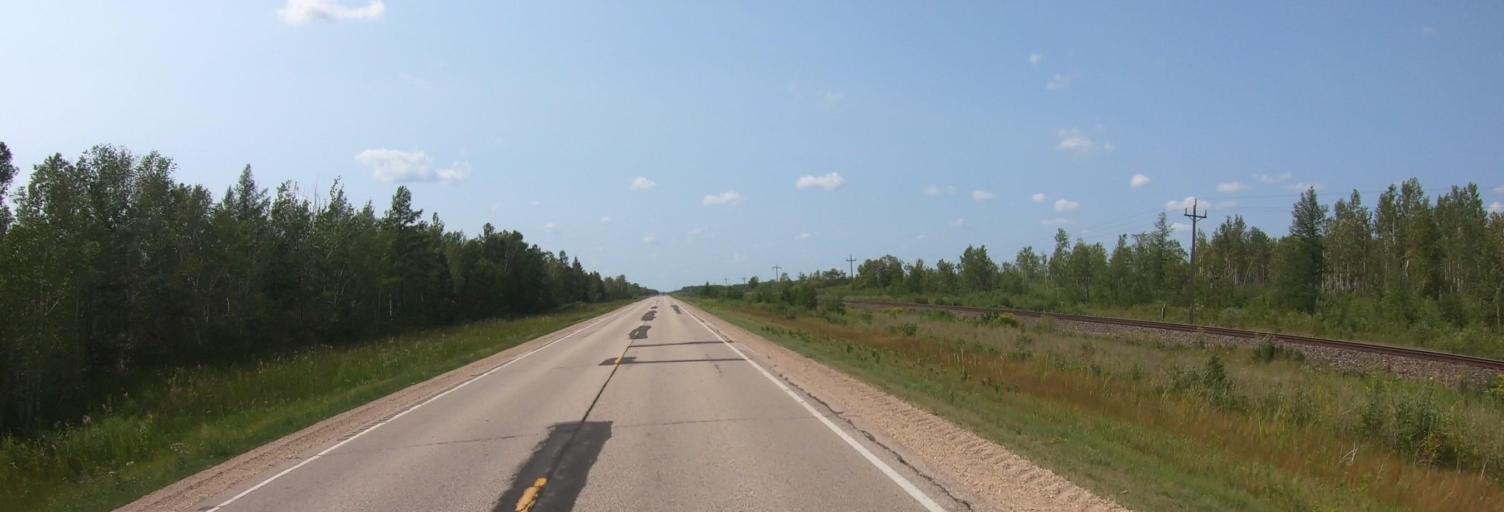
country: US
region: Minnesota
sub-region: Lake of the Woods County
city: Baudette
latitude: 48.7503
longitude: -94.8809
